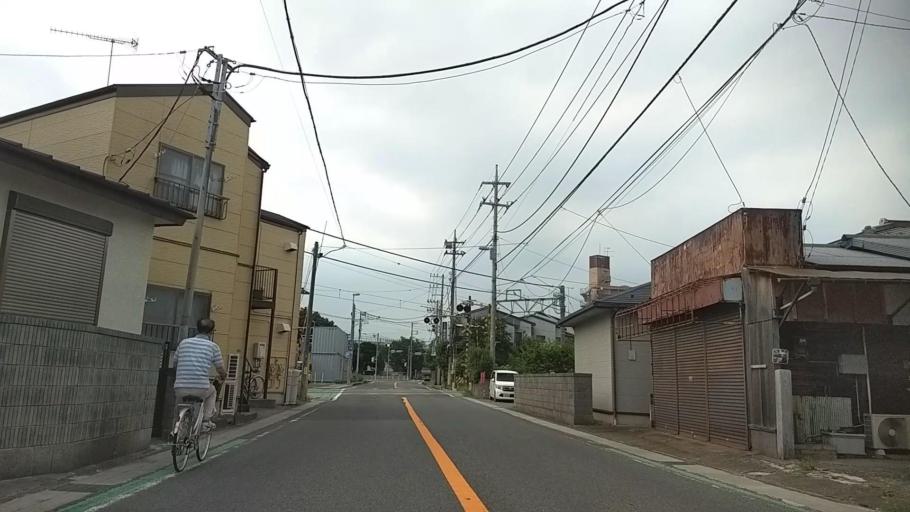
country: JP
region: Kanagawa
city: Atsugi
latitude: 35.4405
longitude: 139.3788
